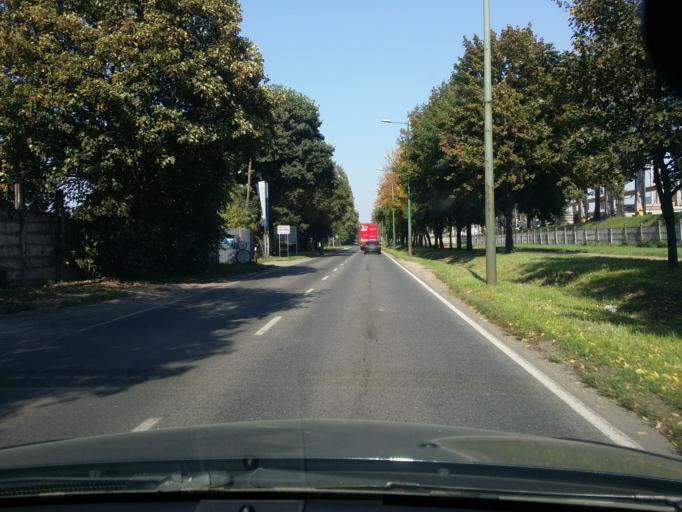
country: HU
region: Fejer
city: Dunaujvaros
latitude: 46.9387
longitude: 18.9517
